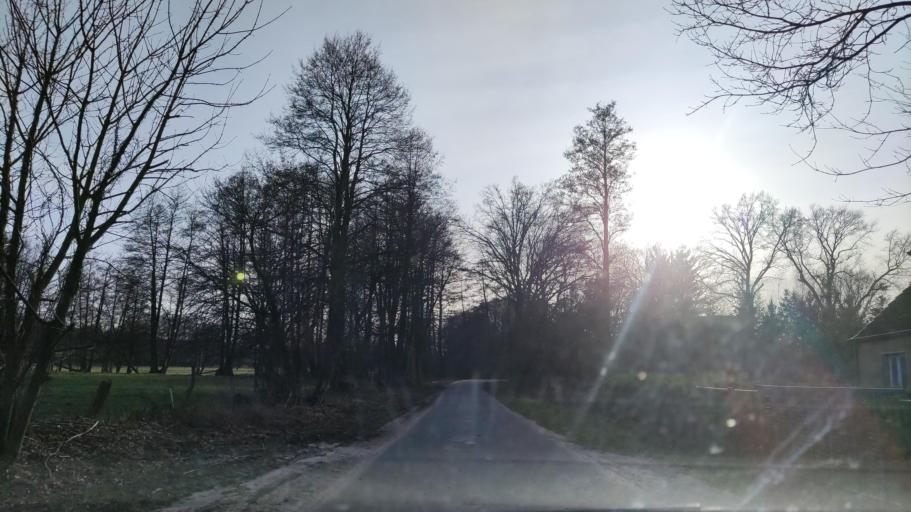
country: DE
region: Schleswig-Holstein
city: Langenlehsten
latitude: 53.4622
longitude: 10.7746
